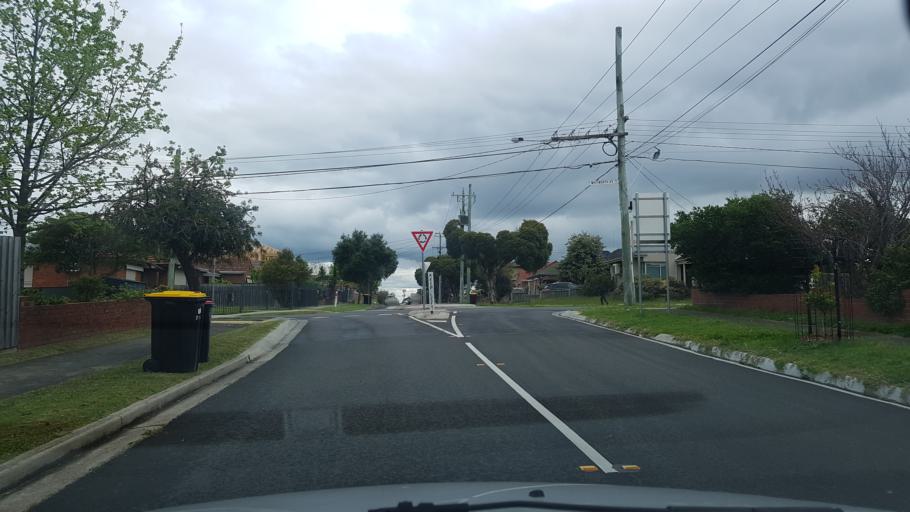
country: AU
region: Victoria
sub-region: Greater Dandenong
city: Springvale
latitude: -37.9403
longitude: 145.1521
